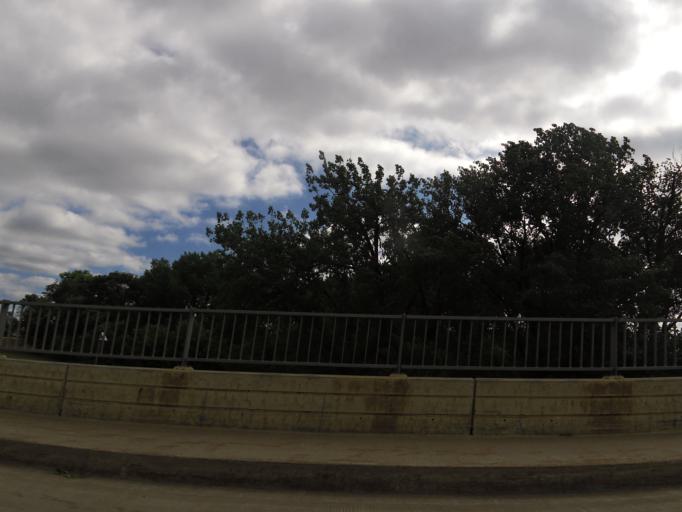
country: US
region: Minnesota
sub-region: Polk County
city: East Grand Forks
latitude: 47.9243
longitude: -97.0164
